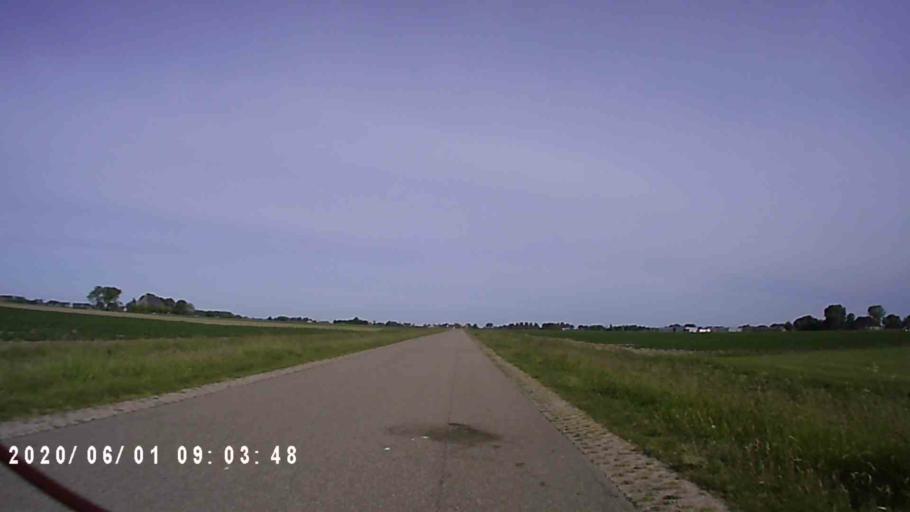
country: NL
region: Friesland
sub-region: Gemeente Ferwerderadiel
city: Hallum
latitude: 53.2946
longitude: 5.7842
